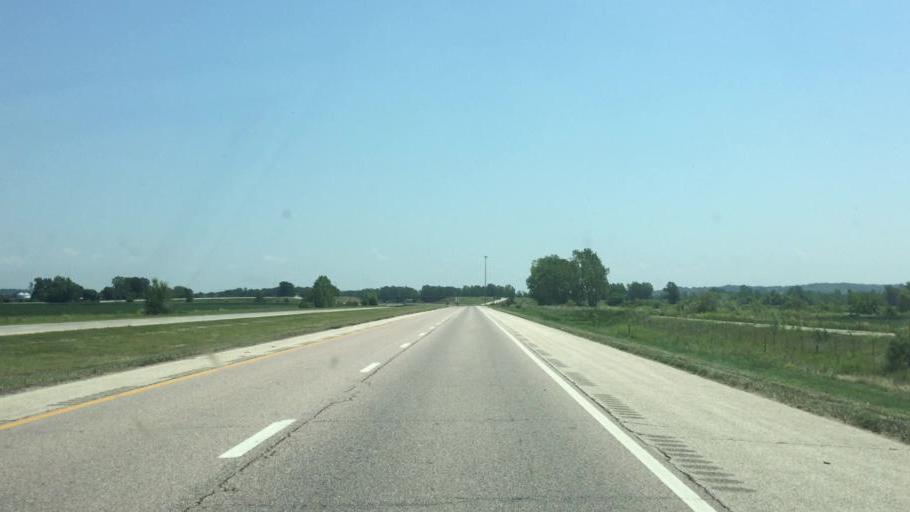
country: US
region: Kansas
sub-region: Doniphan County
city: Elwood
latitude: 39.7404
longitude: -94.9045
